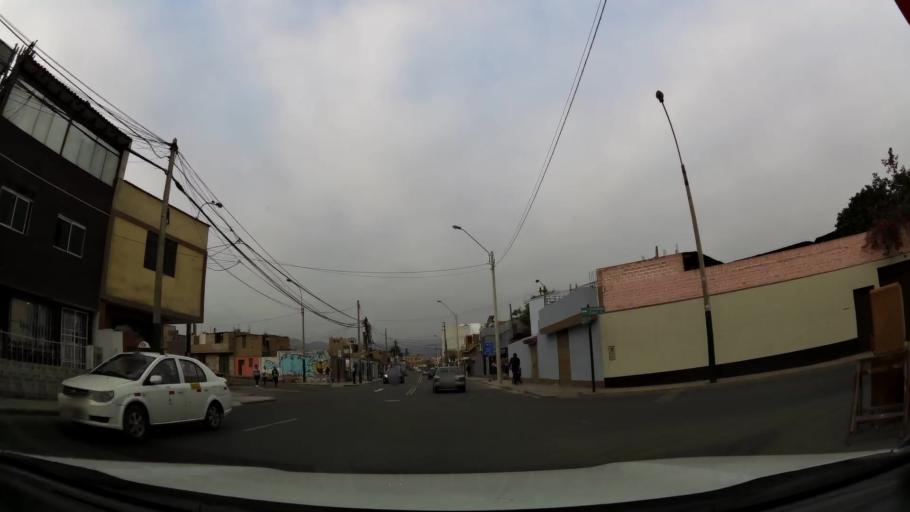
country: PE
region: Lima
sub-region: Lima
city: Surco
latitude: -12.1470
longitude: -77.0110
